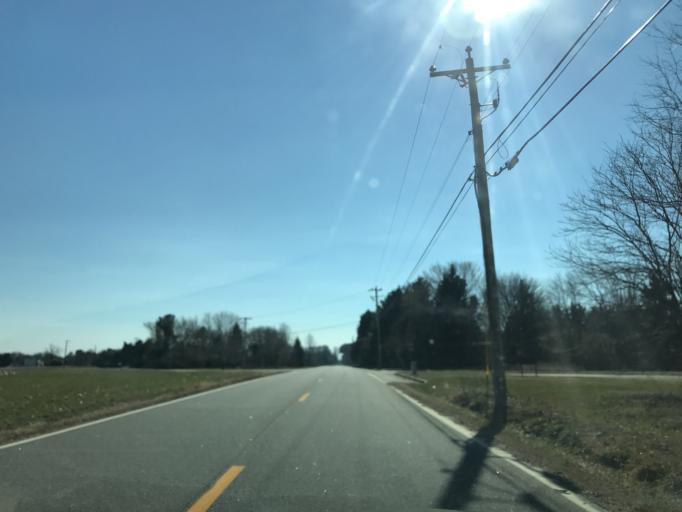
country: US
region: Maryland
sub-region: Queen Anne's County
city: Stevensville
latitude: 39.0098
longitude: -76.3116
